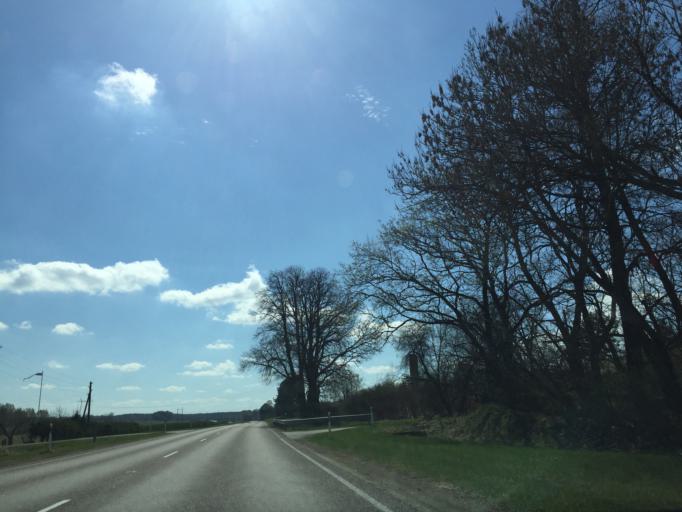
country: EE
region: Valgamaa
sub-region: Torva linn
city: Torva
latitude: 58.0365
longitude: 26.1823
